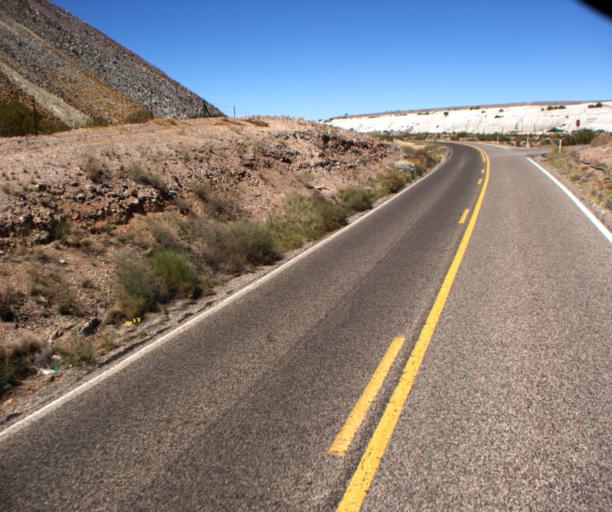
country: US
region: Arizona
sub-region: Pima County
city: Ajo
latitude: 32.3657
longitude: -112.8386
